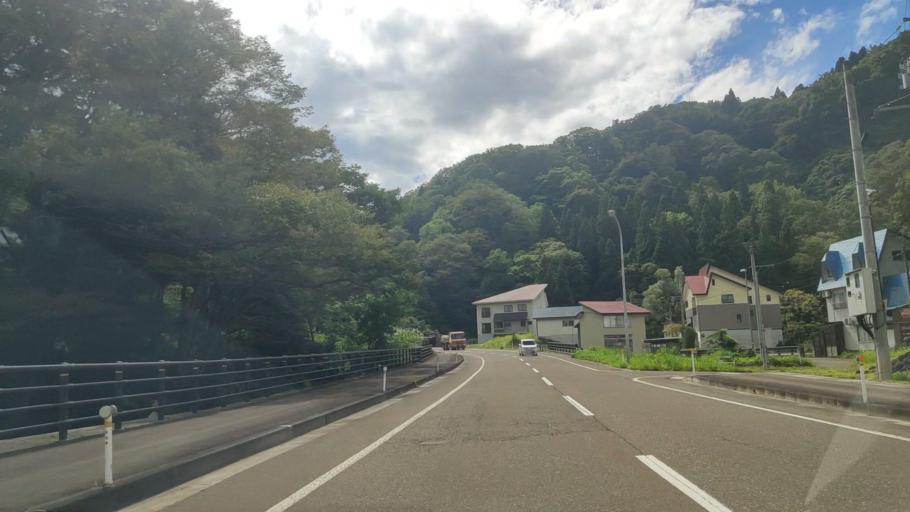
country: JP
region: Niigata
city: Arai
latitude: 36.9536
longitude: 138.2775
